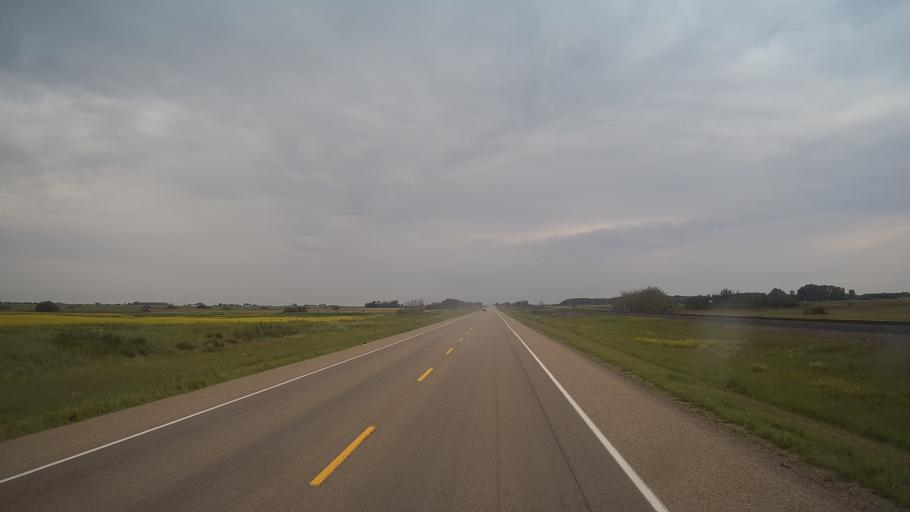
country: CA
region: Saskatchewan
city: Langham
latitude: 52.1273
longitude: -107.2600
